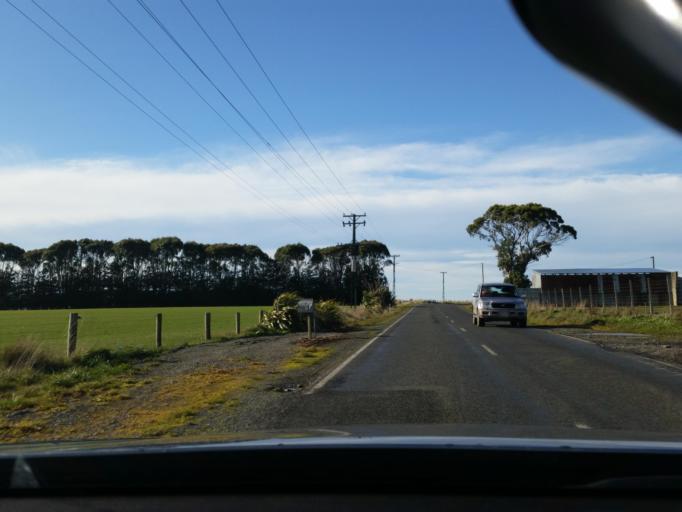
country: NZ
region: Southland
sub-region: Southland District
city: Riverton
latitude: -46.1483
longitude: 168.0324
